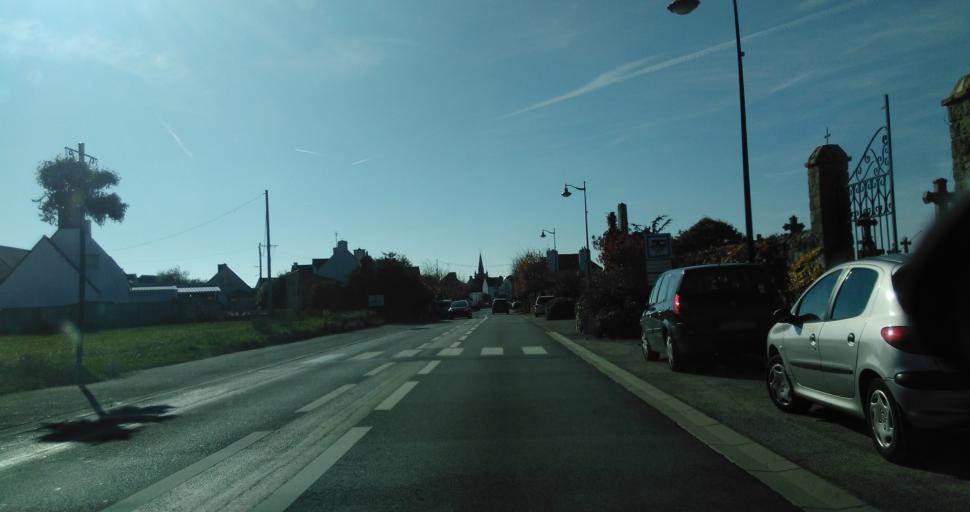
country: FR
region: Brittany
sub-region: Departement du Morbihan
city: Plouharnel
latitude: 47.6003
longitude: -3.1095
